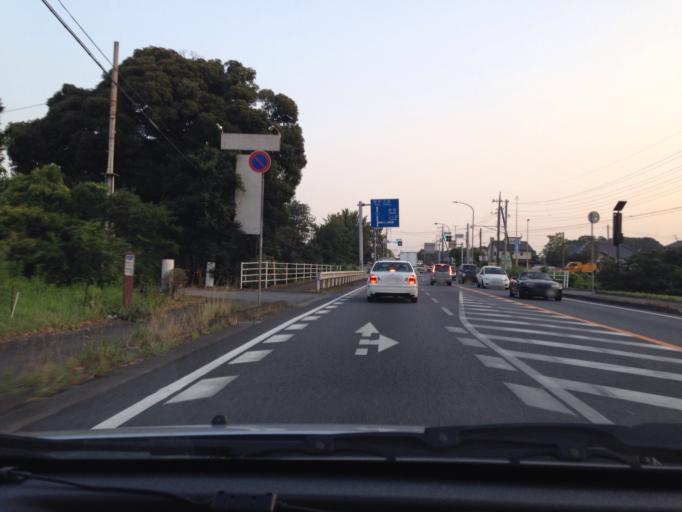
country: JP
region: Ibaraki
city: Ishioka
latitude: 36.1618
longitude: 140.2463
